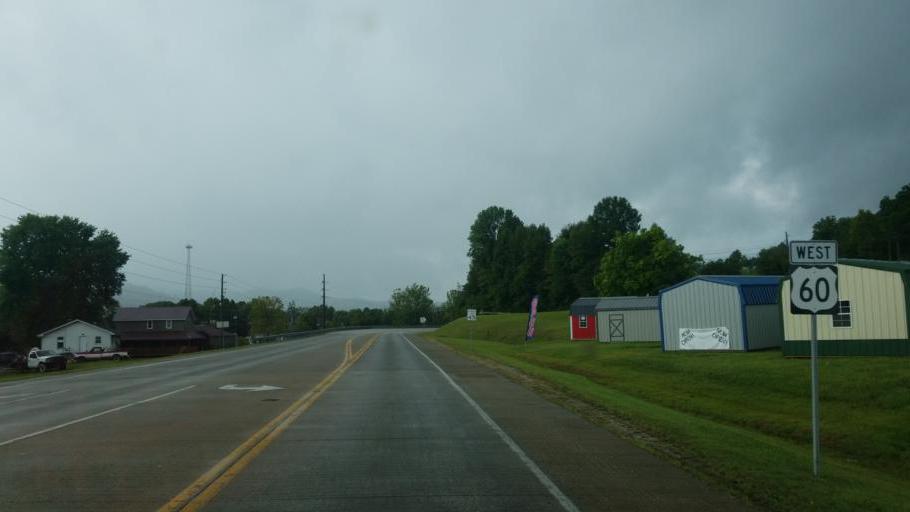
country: US
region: Kentucky
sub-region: Rowan County
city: Morehead
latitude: 38.1696
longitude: -83.4396
